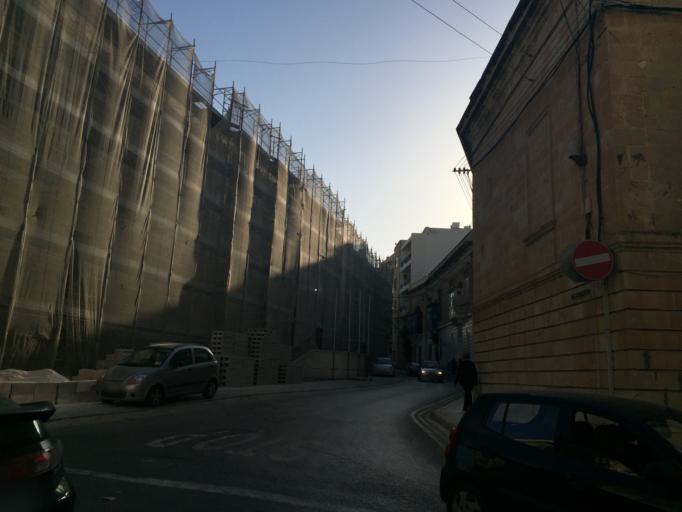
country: MT
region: Tas-Sliema
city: Sliema
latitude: 35.9122
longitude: 14.5018
